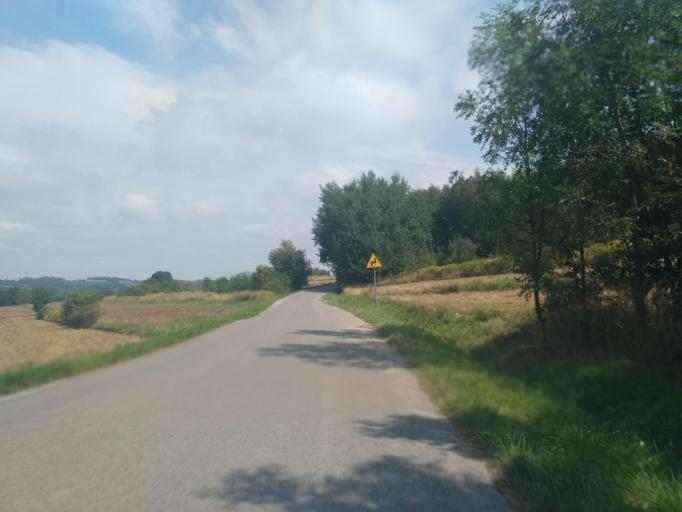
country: PL
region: Subcarpathian Voivodeship
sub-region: Powiat lancucki
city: Kraczkowa
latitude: 50.0260
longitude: 22.1539
